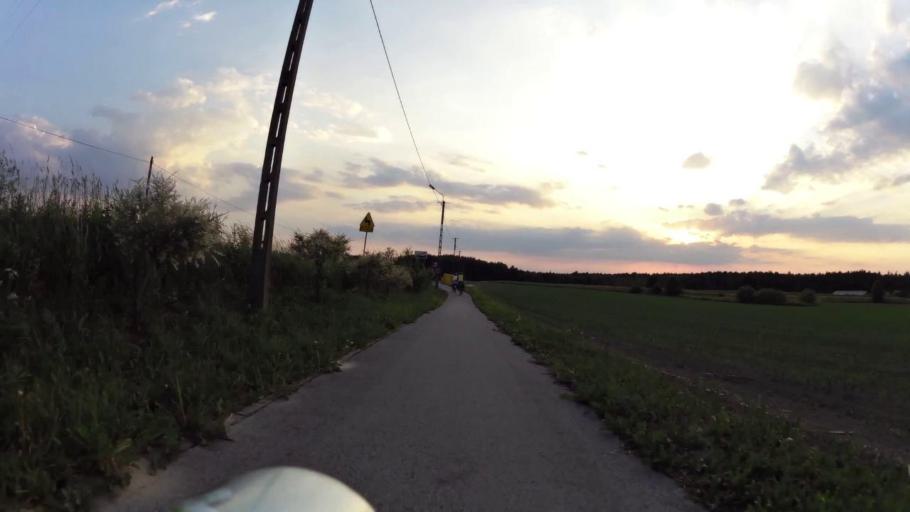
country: PL
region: Kujawsko-Pomorskie
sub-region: Powiat bydgoski
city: Dabrowa Chelminska
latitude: 53.1792
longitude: 18.2932
